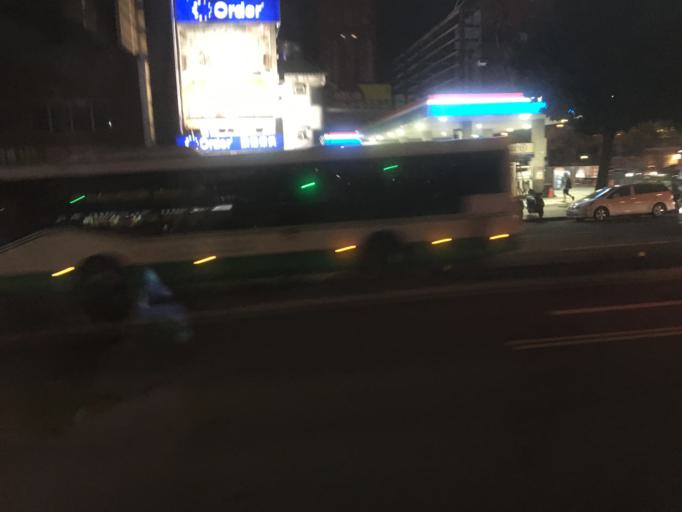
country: TW
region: Taiwan
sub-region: Taoyuan
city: Taoyuan
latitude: 25.0574
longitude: 121.3647
